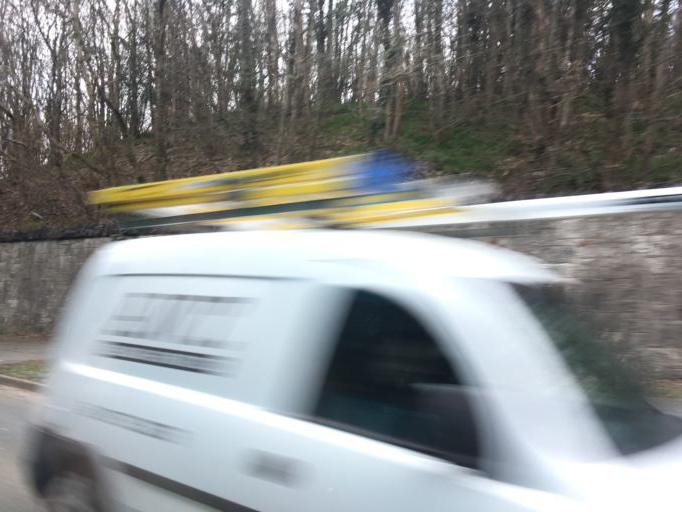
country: GB
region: Wales
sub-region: Gwynedd
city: Y Felinheli
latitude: 53.1944
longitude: -4.1868
